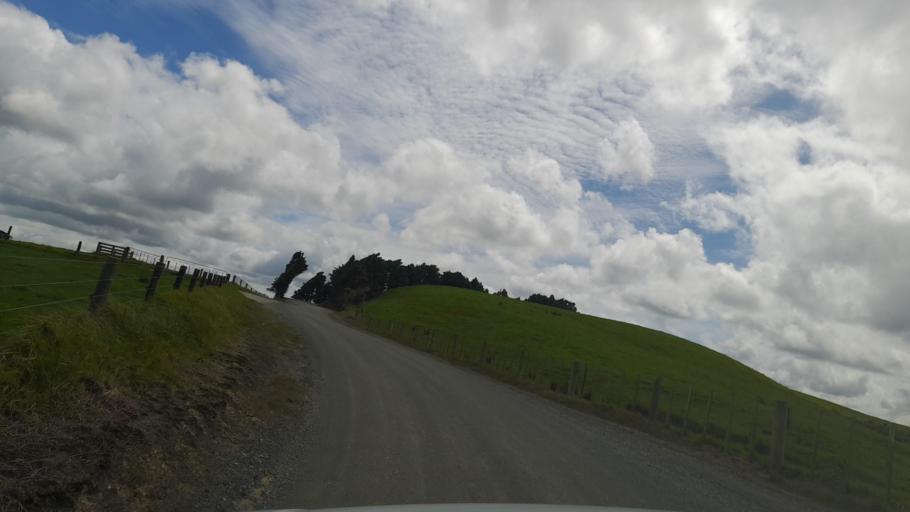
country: NZ
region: Auckland
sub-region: Auckland
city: Wellsford
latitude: -36.1900
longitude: 174.3398
